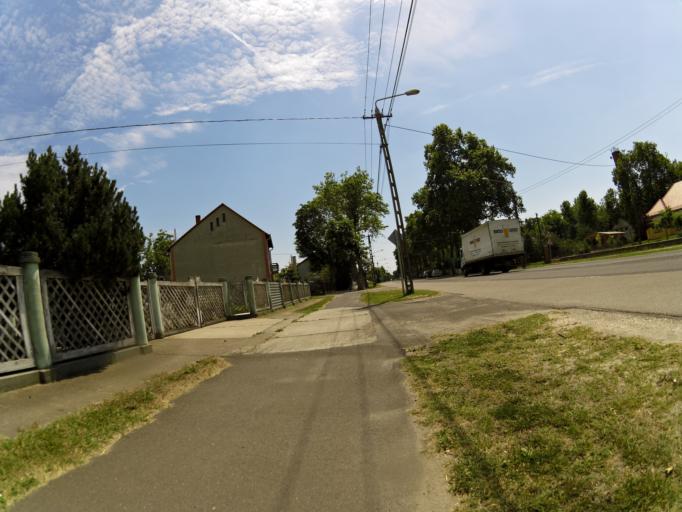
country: HU
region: Csongrad
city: Balastya
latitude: 46.4249
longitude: 20.0128
